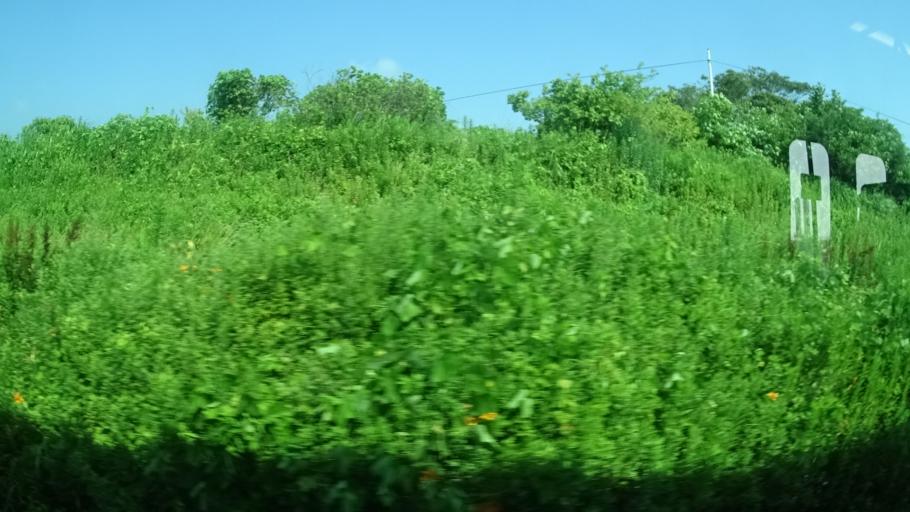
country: JP
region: Fukushima
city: Namie
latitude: 37.3277
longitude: 141.0221
